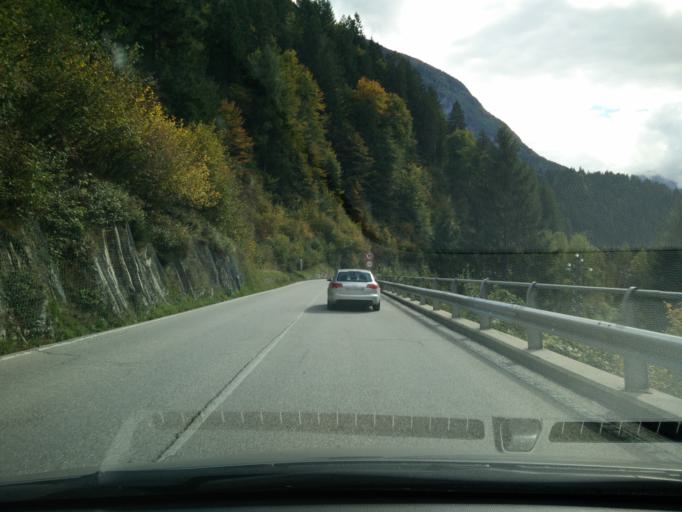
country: IT
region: Veneto
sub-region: Provincia di Belluno
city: Vigo di Cadore
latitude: 46.5378
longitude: 12.4663
